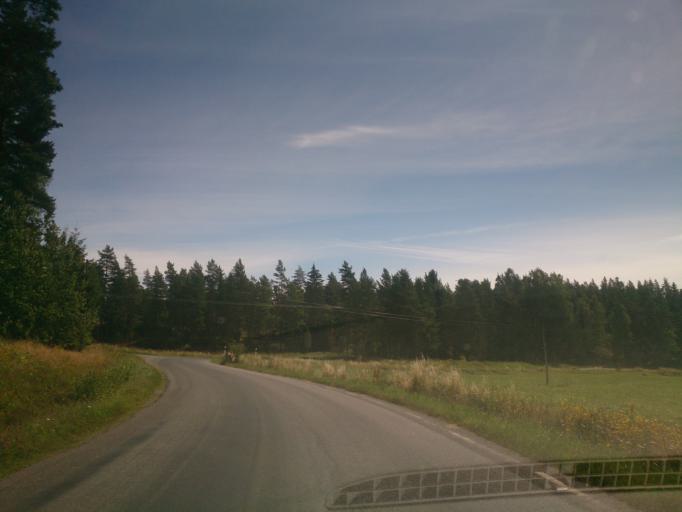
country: SE
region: OEstergoetland
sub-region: Valdemarsviks Kommun
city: Valdemarsvik
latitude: 58.2962
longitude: 16.6671
